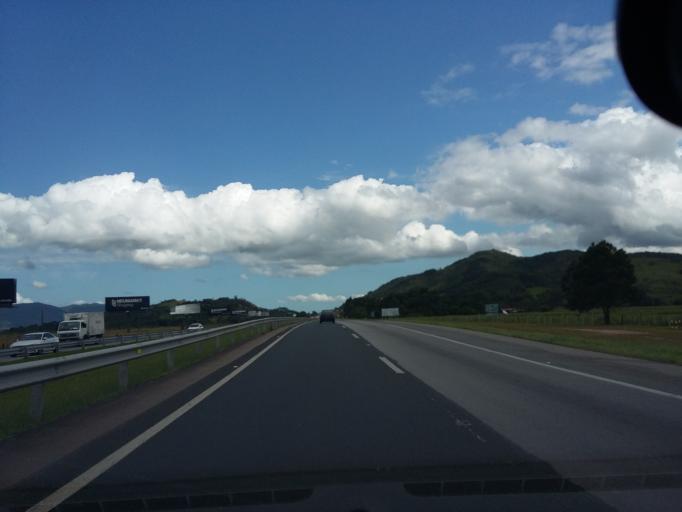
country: BR
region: Santa Catarina
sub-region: Tijucas
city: Tijucas
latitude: -27.2672
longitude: -48.6319
